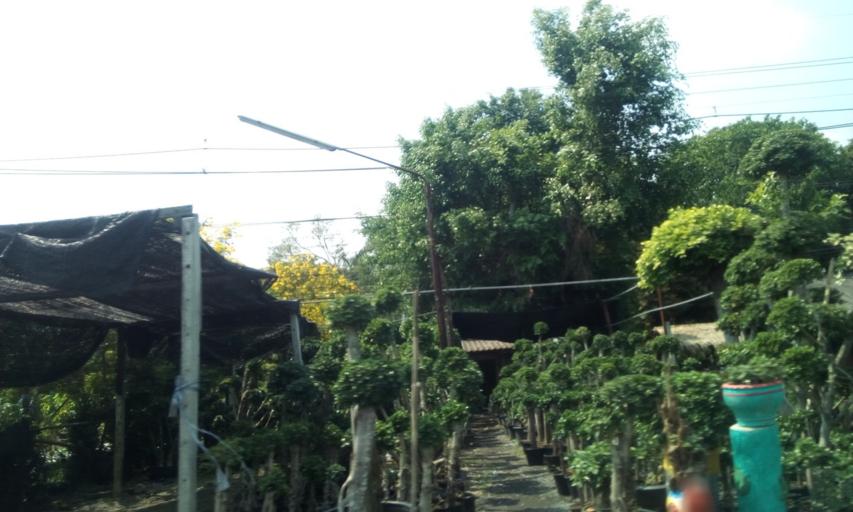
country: TH
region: Nakhon Nayok
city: Ongkharak
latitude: 14.1111
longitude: 100.9435
